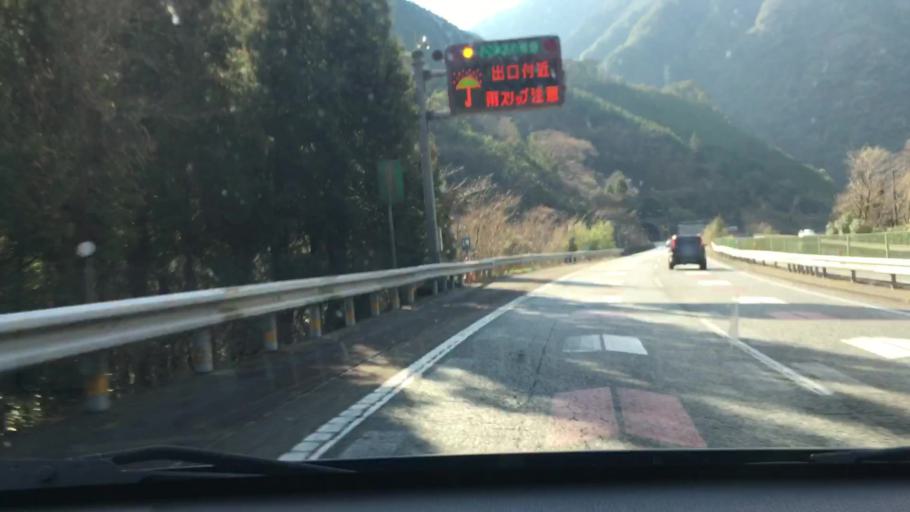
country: JP
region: Kumamoto
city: Hitoyoshi
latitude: 32.3172
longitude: 130.7544
